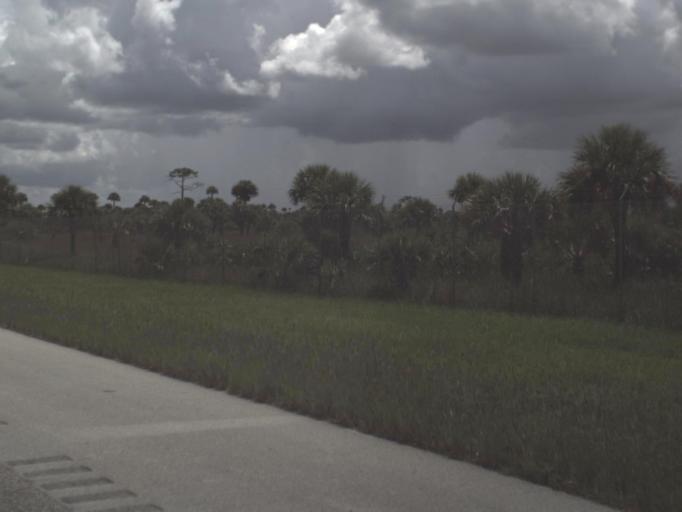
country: US
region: Florida
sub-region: Collier County
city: Immokalee
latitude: 26.1547
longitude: -81.3335
